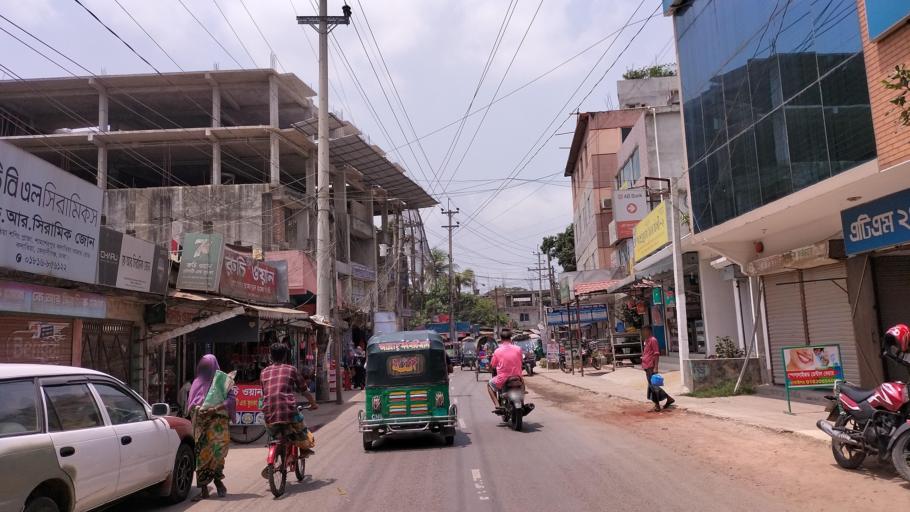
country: BD
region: Dhaka
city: Azimpur
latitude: 23.7311
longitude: 90.2755
